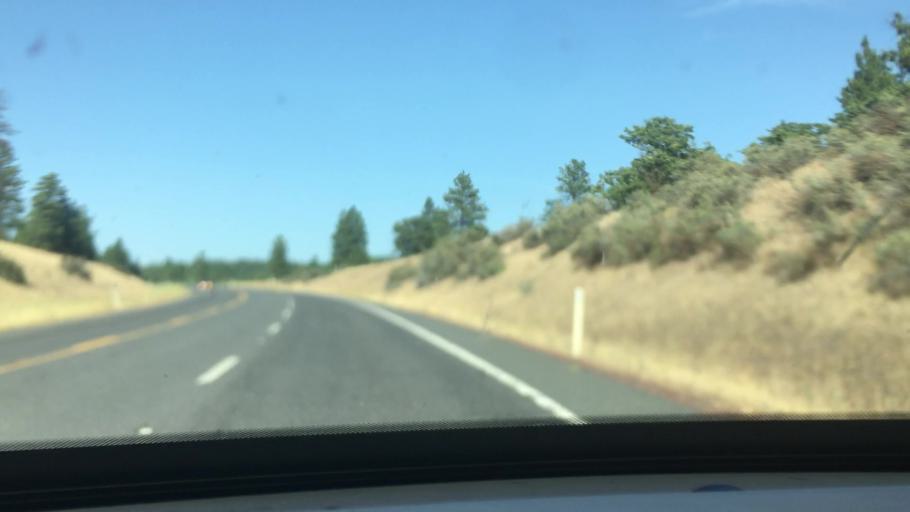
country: US
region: Washington
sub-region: Klickitat County
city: Goldendale
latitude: 45.8873
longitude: -120.7363
